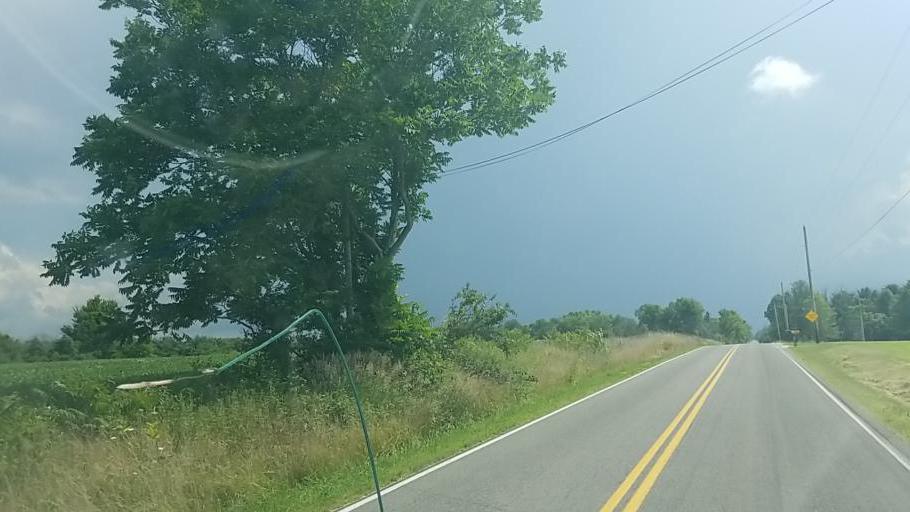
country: US
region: Ohio
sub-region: Medina County
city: Lodi
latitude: 41.0882
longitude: -82.0043
